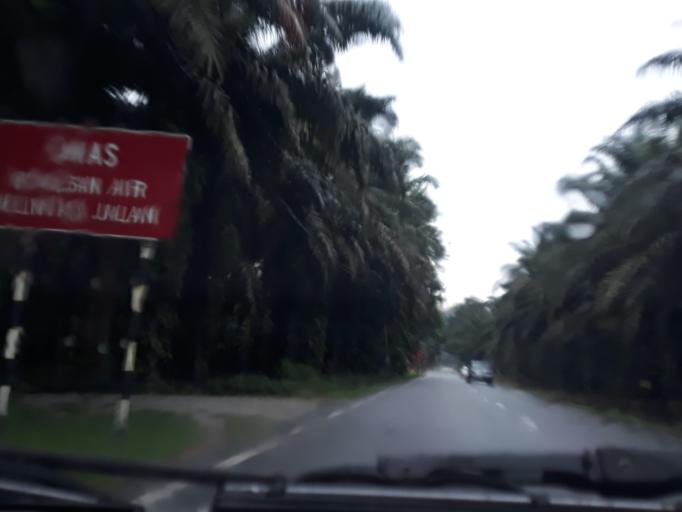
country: MY
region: Kedah
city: Kulim
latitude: 5.2332
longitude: 100.6039
